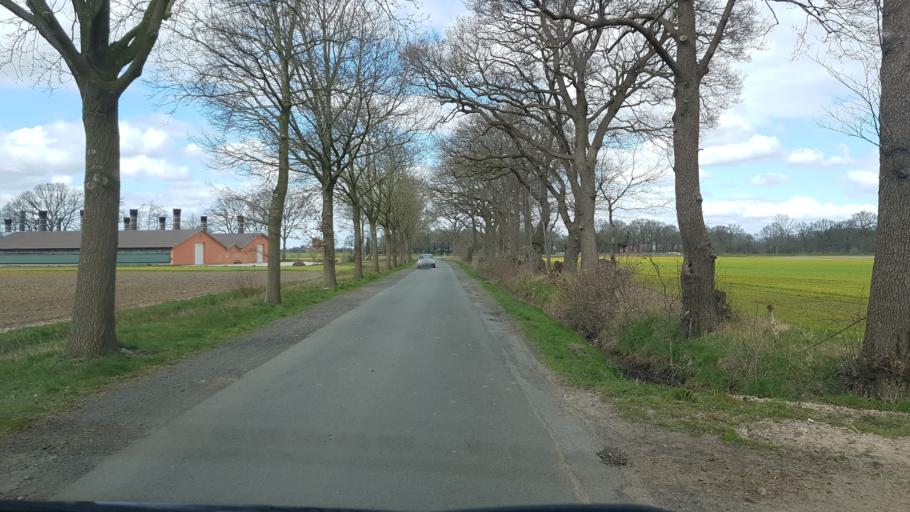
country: DE
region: Lower Saxony
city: Edewecht
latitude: 53.1082
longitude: 7.9436
